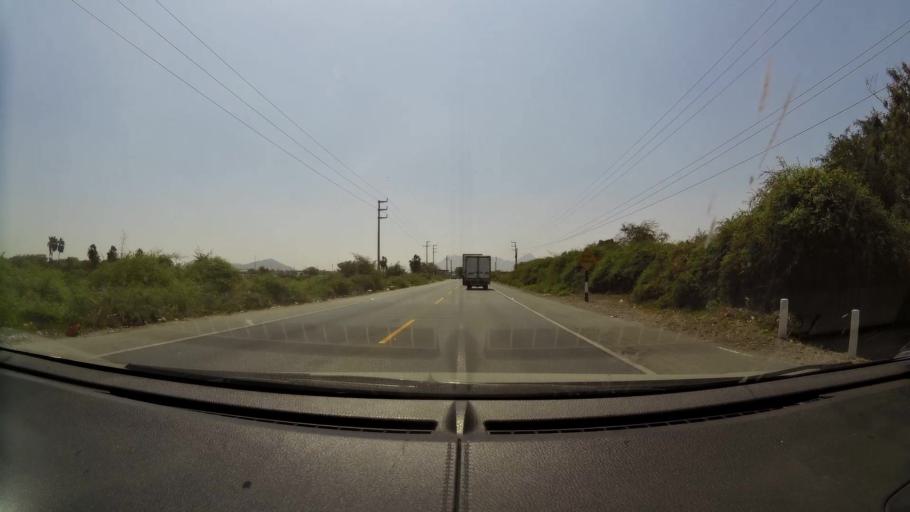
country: PE
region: Lambayeque
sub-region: Provincia de Chiclayo
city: Mocupe
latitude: -6.9952
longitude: -79.6183
